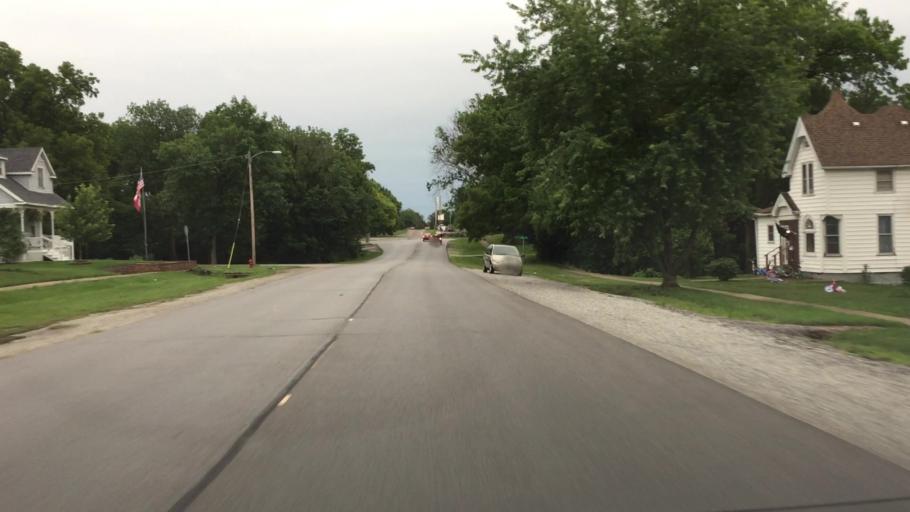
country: US
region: Illinois
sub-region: Hancock County
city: Hamilton
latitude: 40.3931
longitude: -91.3418
